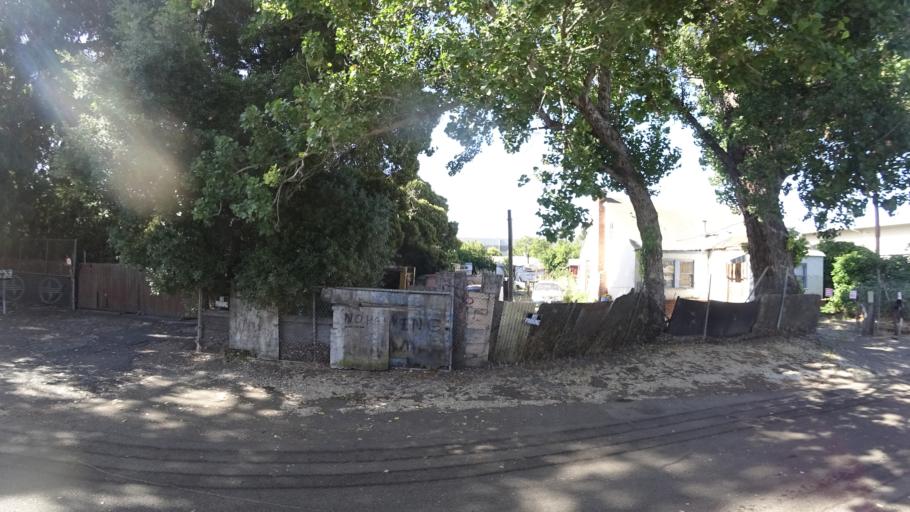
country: US
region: California
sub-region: Alameda County
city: San Lorenzo
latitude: 37.6448
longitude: -122.1280
